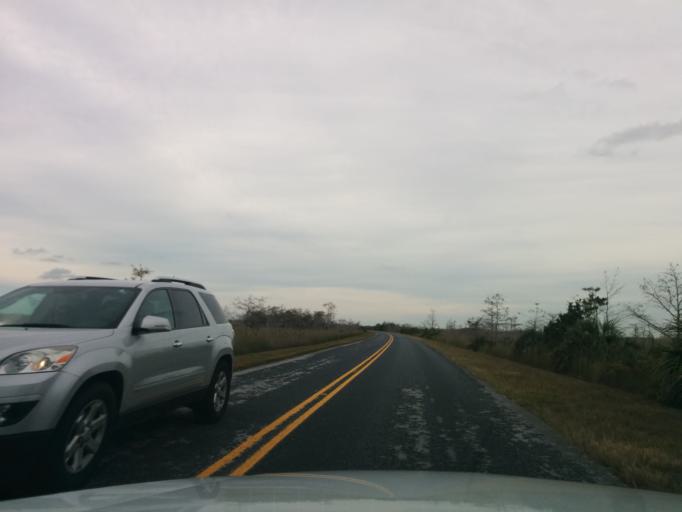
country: US
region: Florida
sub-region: Miami-Dade County
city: Florida City
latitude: 25.4331
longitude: -80.7592
